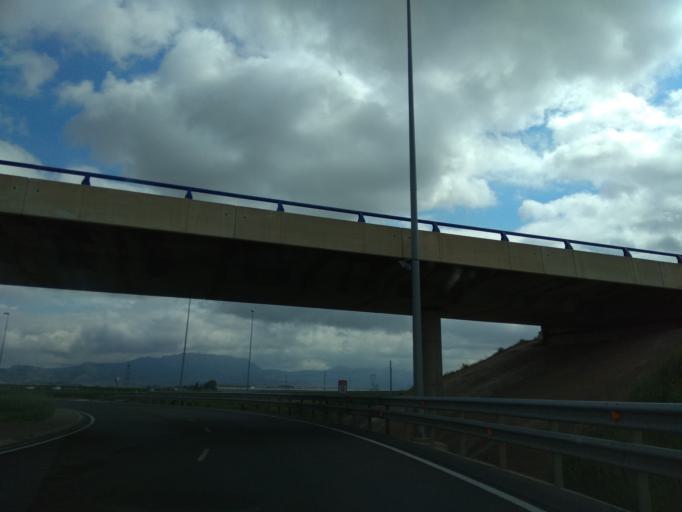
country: ES
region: La Rioja
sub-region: Provincia de La Rioja
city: Casalarreina
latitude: 42.5541
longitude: -2.8975
